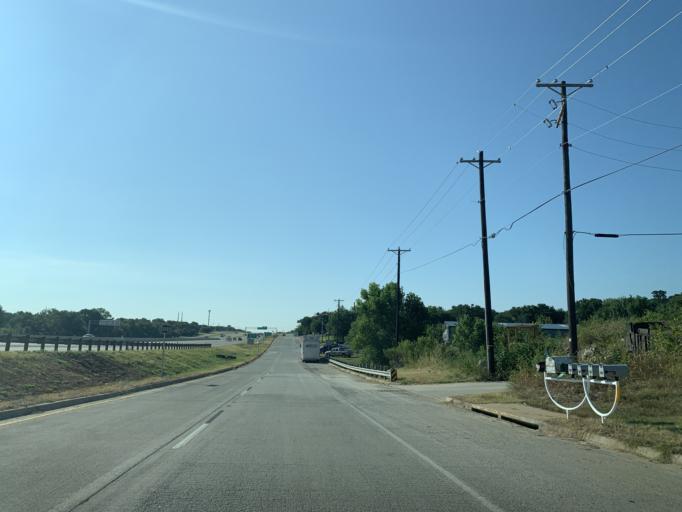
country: US
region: Texas
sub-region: Tarrant County
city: Lakeside
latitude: 32.8350
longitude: -97.4893
